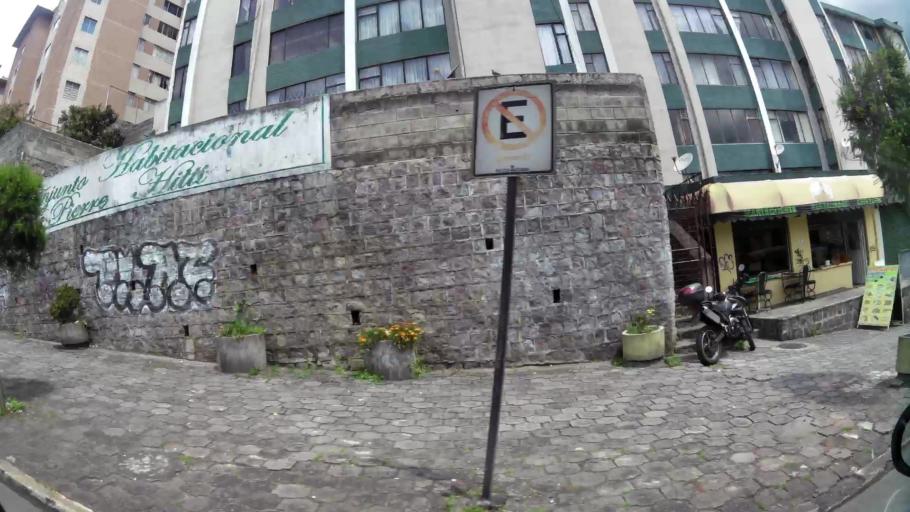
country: EC
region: Pichincha
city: Quito
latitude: -0.2355
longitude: -78.5097
